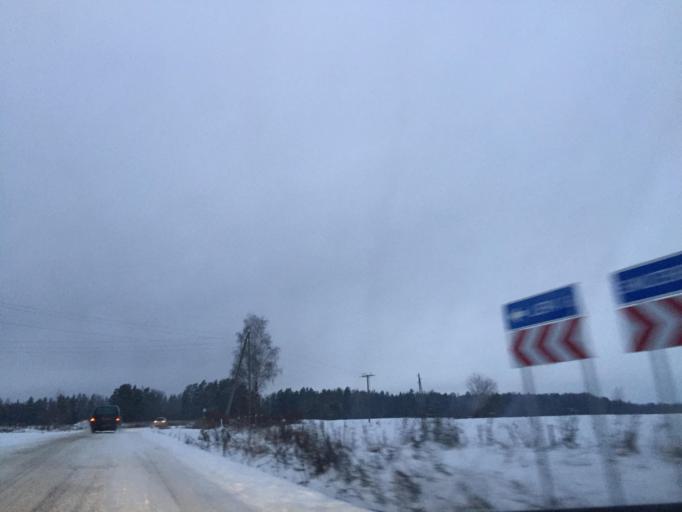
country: LV
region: Raunas
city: Rauna
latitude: 57.4263
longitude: 25.6575
